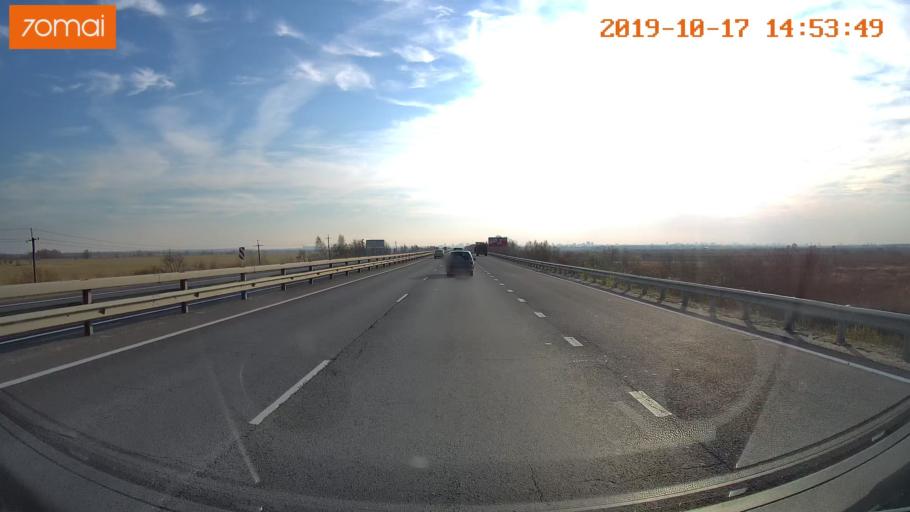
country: RU
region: Rjazan
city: Polyany
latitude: 54.6895
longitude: 39.8363
